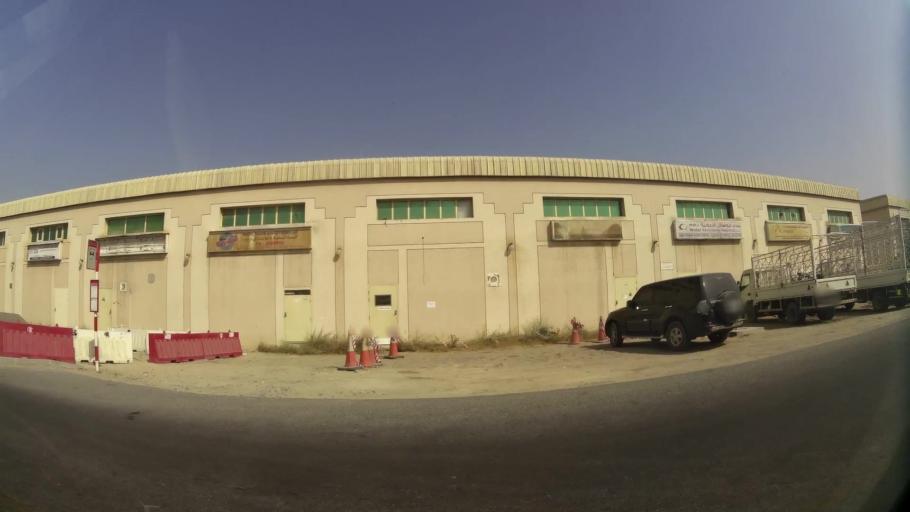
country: AE
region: Ash Shariqah
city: Sharjah
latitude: 25.2974
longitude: 55.3895
